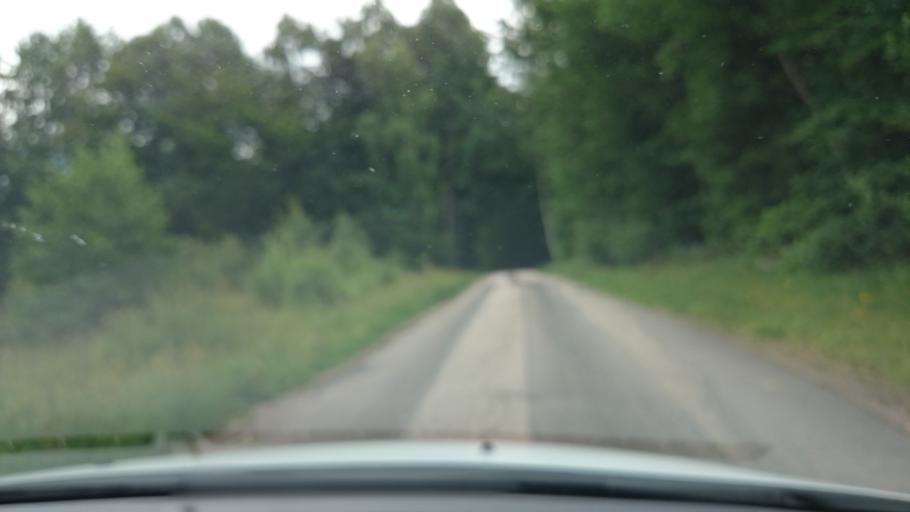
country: SE
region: Halland
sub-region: Hylte Kommun
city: Hyltebruk
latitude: 56.9839
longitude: 13.2352
